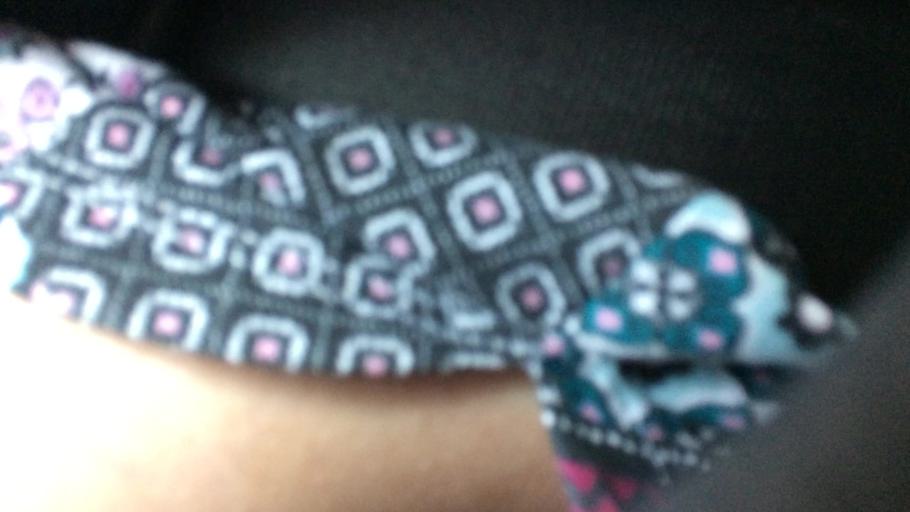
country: US
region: New Mexico
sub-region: Colfax County
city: Springer
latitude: 36.2401
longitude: -104.6511
